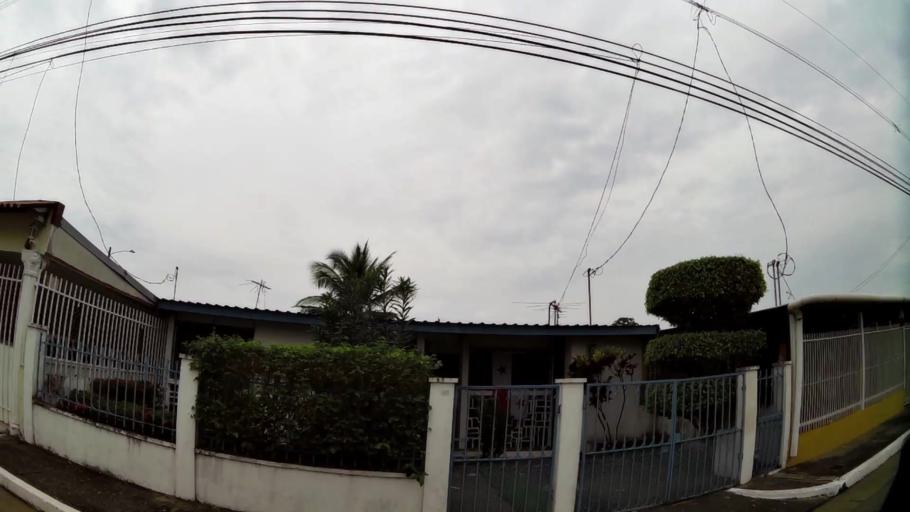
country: PA
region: Panama
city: San Miguelito
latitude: 9.0468
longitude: -79.4469
